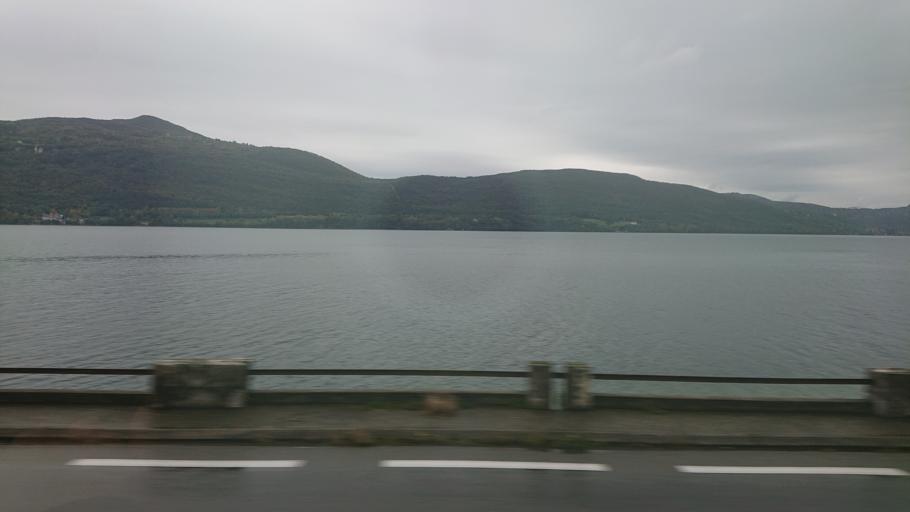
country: FR
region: Rhone-Alpes
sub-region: Departement de la Savoie
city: Chatillon
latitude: 45.7652
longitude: 5.8705
